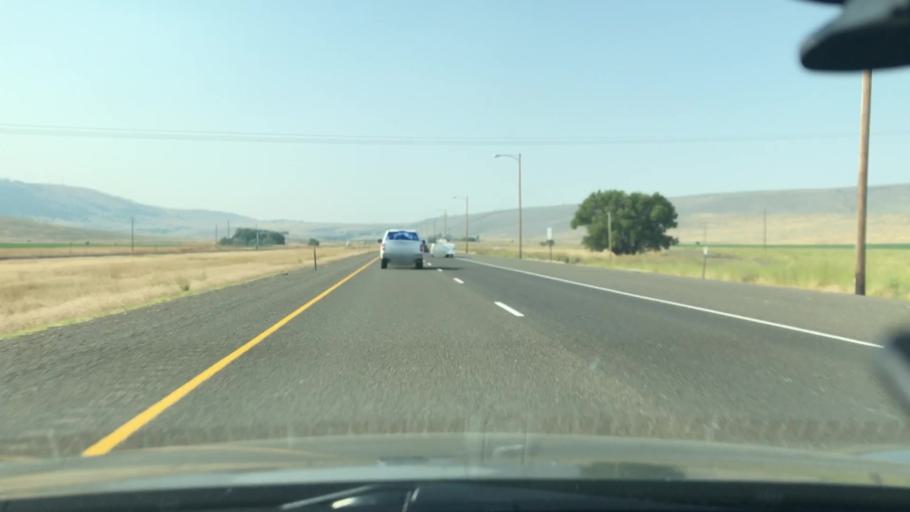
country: US
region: Oregon
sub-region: Union County
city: Union
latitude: 45.1116
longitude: -117.9580
